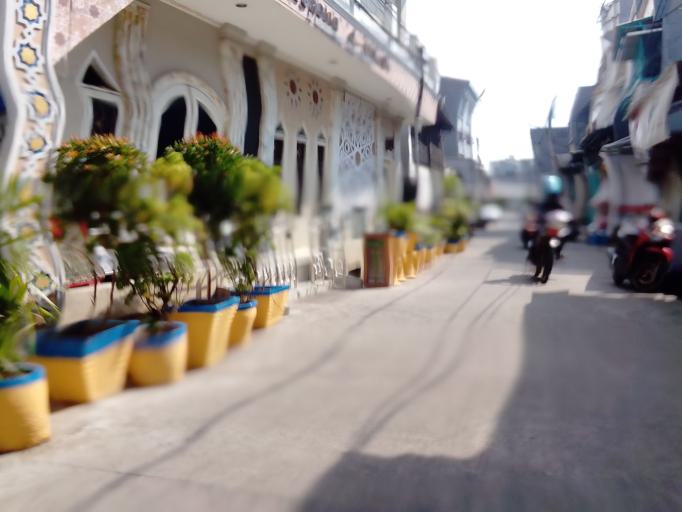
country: ID
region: Jakarta Raya
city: Jakarta
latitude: -6.1499
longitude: 106.8131
